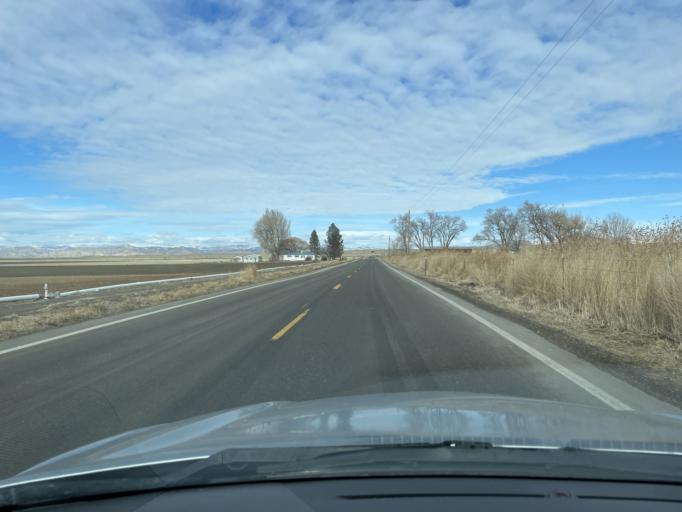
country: US
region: Colorado
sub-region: Mesa County
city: Loma
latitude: 39.2565
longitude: -108.8128
